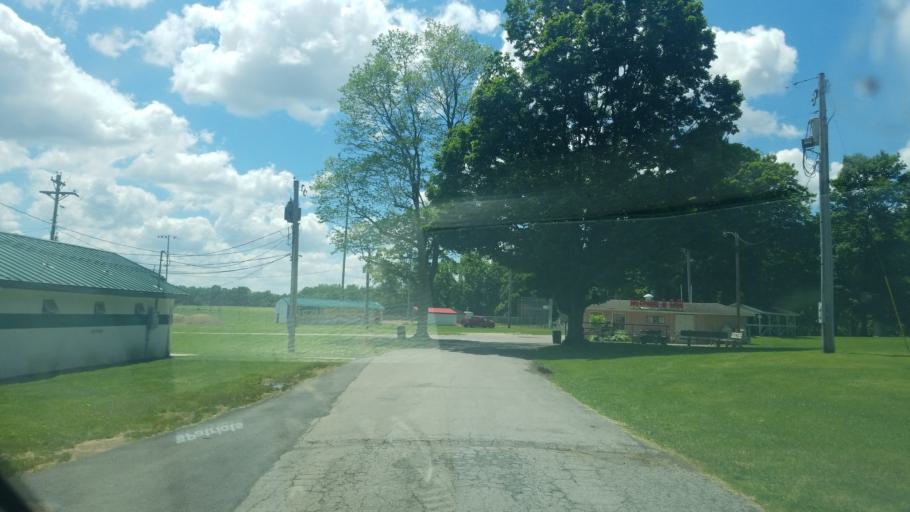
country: US
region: Ohio
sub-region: Huron County
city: New London
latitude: 41.0803
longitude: -82.4052
